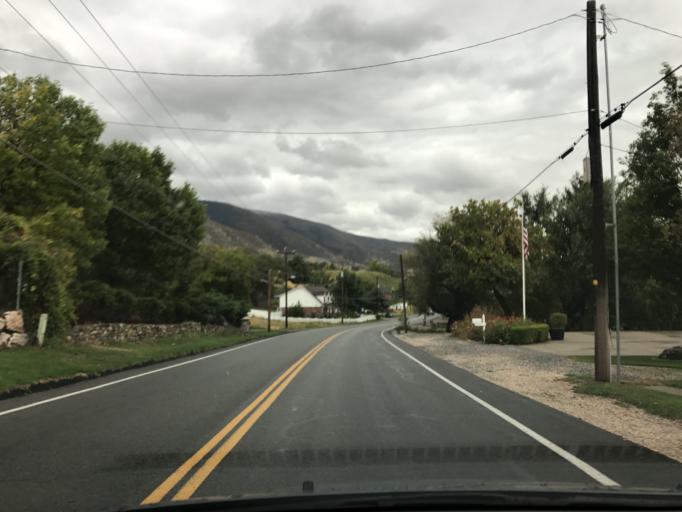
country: US
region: Utah
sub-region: Davis County
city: Farmington
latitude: 40.9994
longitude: -111.8991
